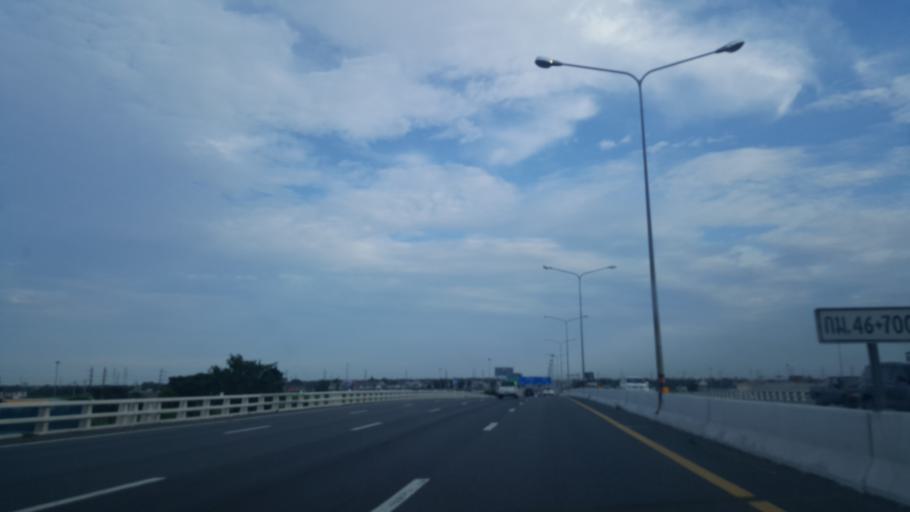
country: TH
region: Chachoengsao
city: Bang Pakong
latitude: 13.5576
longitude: 100.9935
